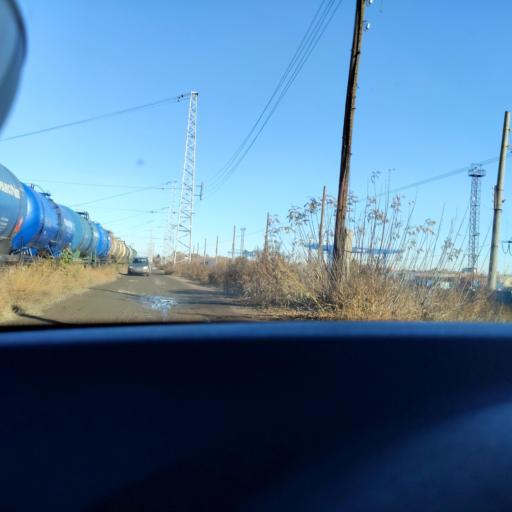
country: RU
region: Samara
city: Samara
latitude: 53.2043
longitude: 50.2501
